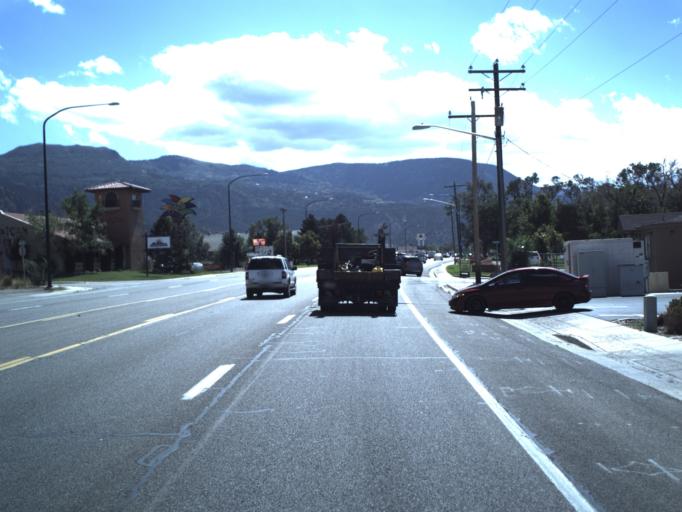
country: US
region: Utah
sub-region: Iron County
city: Cedar City
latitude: 37.6933
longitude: -113.0623
